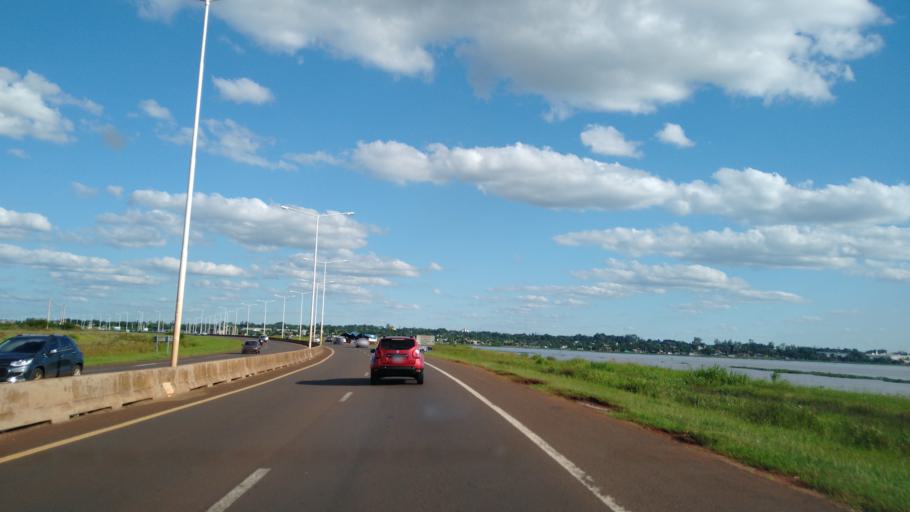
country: AR
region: Misiones
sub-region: Departamento de Capital
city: Posadas
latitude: -27.4085
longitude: -55.8914
